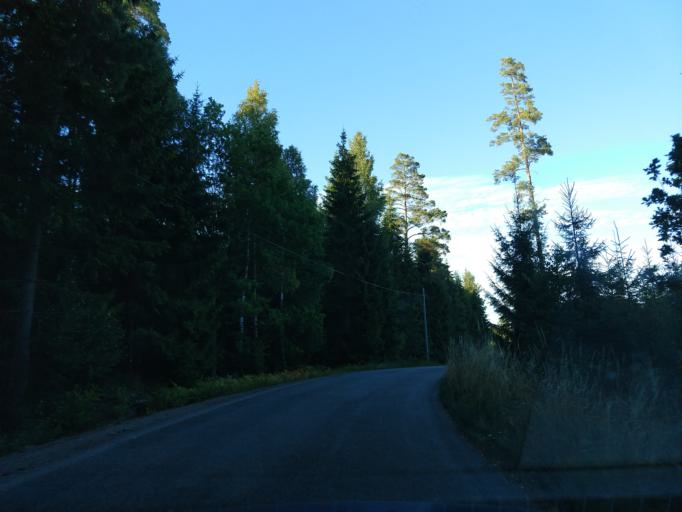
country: SE
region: Blekinge
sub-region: Ronneby Kommun
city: Brakne-Hoby
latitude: 56.2647
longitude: 15.1432
